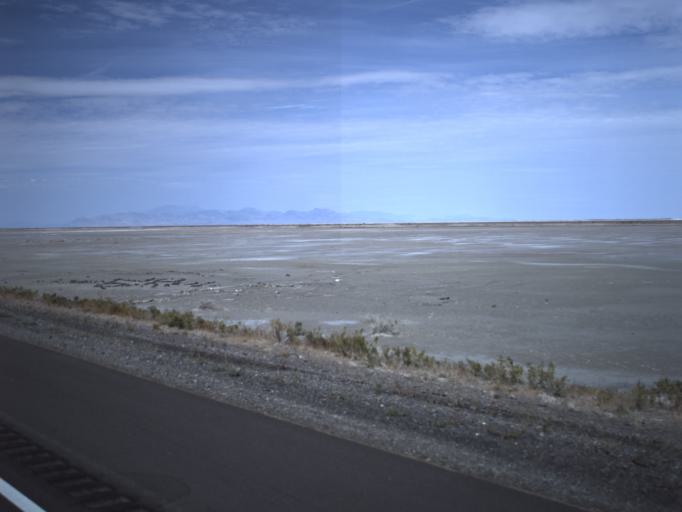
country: US
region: Utah
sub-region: Tooele County
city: Wendover
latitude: 40.7283
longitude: -113.3171
